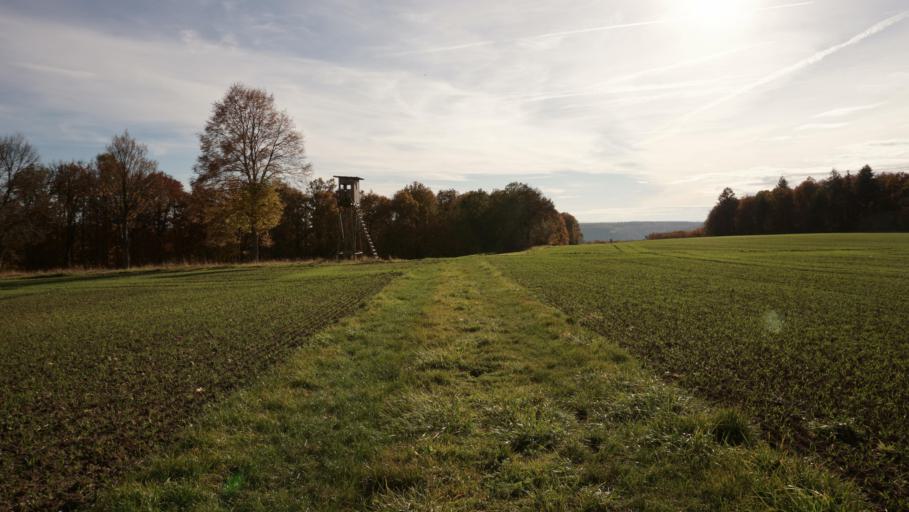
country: DE
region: Baden-Wuerttemberg
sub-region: Karlsruhe Region
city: Hassmersheim
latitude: 49.3149
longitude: 9.1601
